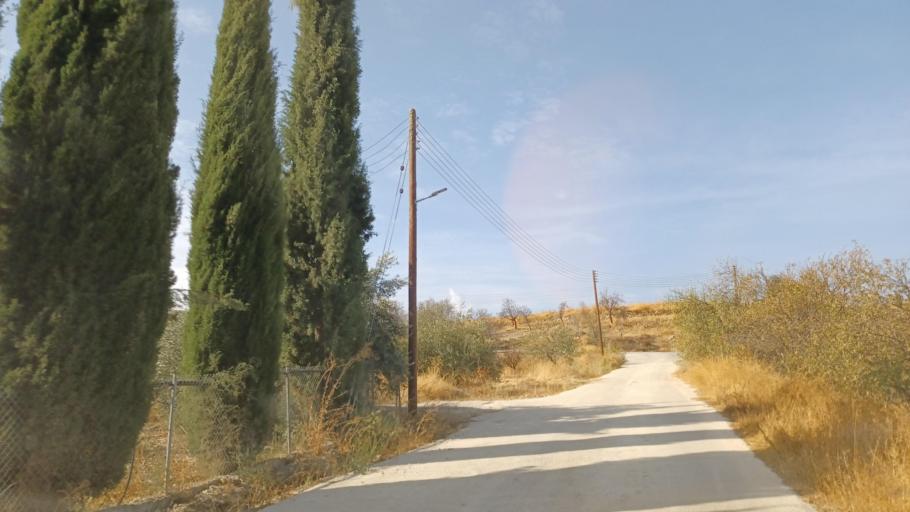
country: CY
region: Pafos
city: Polis
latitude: 34.9544
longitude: 32.5124
